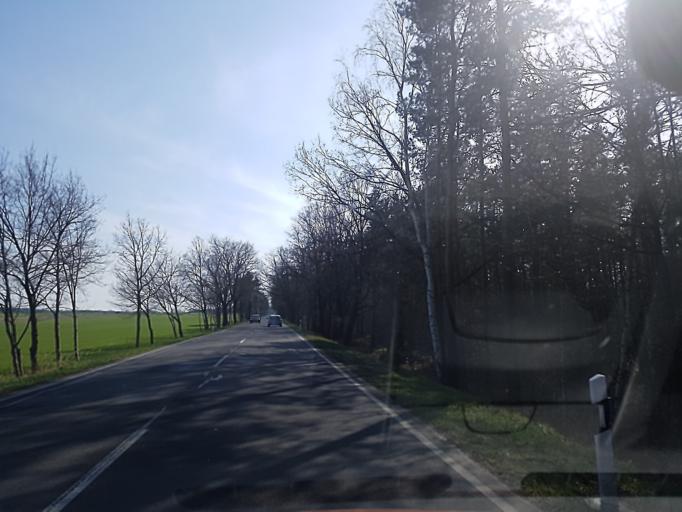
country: DE
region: Brandenburg
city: Calau
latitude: 51.7355
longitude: 13.9368
